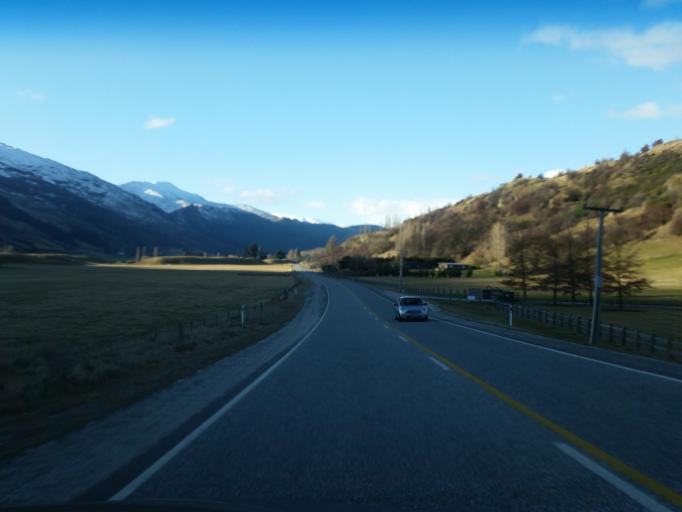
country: NZ
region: Otago
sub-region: Queenstown-Lakes District
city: Queenstown
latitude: -44.9673
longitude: 168.7075
